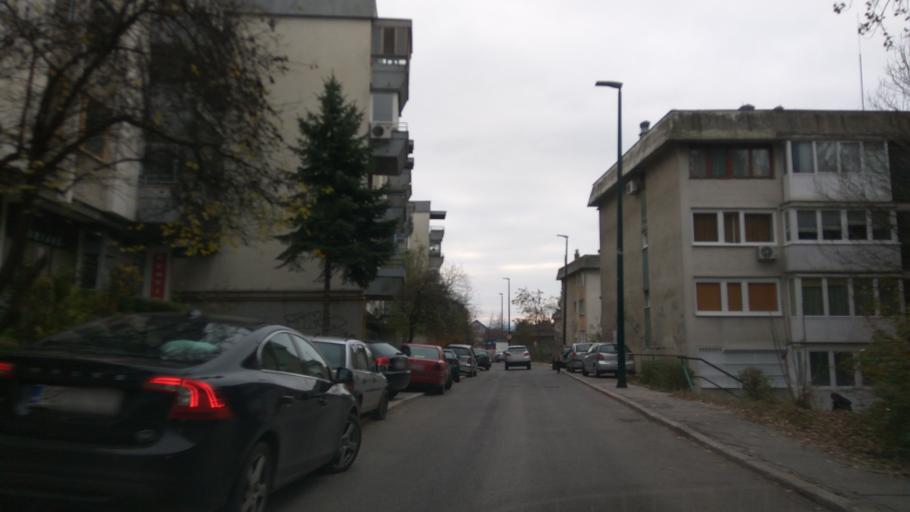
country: BA
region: Federation of Bosnia and Herzegovina
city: Kobilja Glava
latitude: 43.8686
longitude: 18.4046
